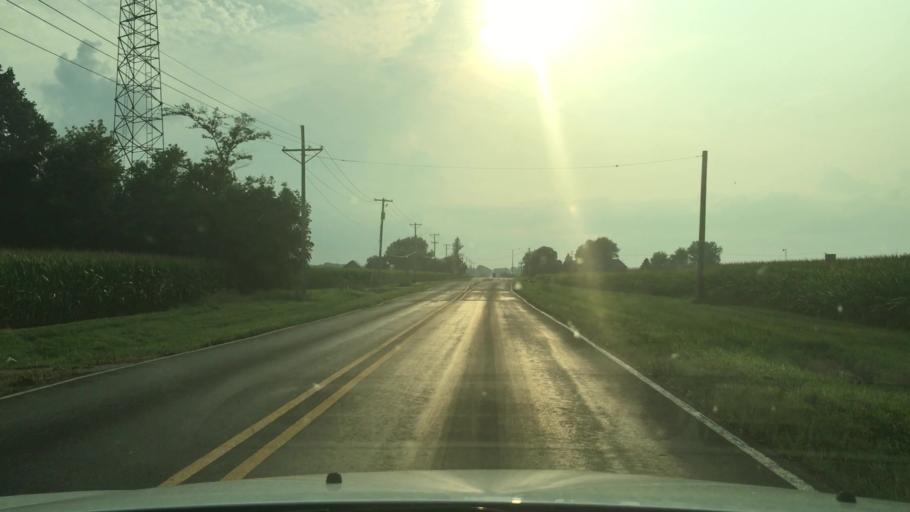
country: US
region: Illinois
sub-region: Ogle County
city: Rochelle
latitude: 41.9200
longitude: -89.0289
